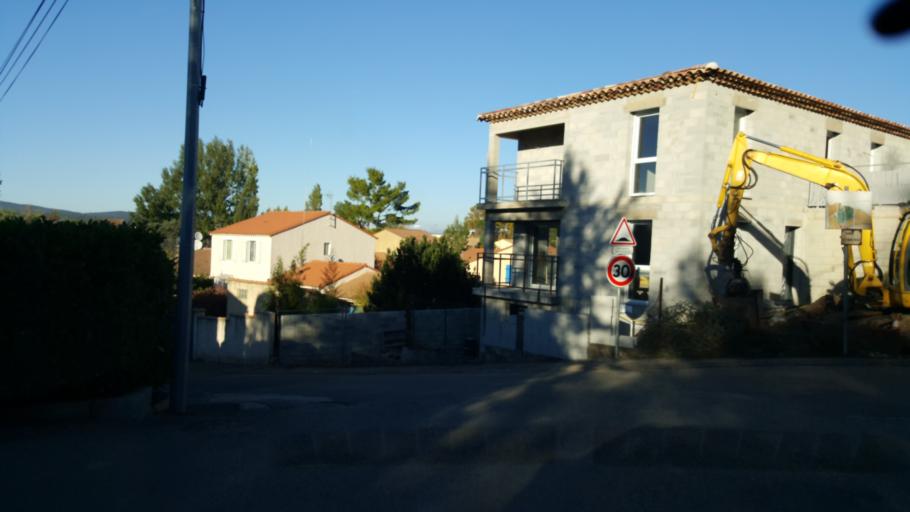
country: FR
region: Provence-Alpes-Cote d'Azur
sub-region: Departement du Var
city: Saint-Maximin-la-Sainte-Baume
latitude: 43.4533
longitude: 5.8503
